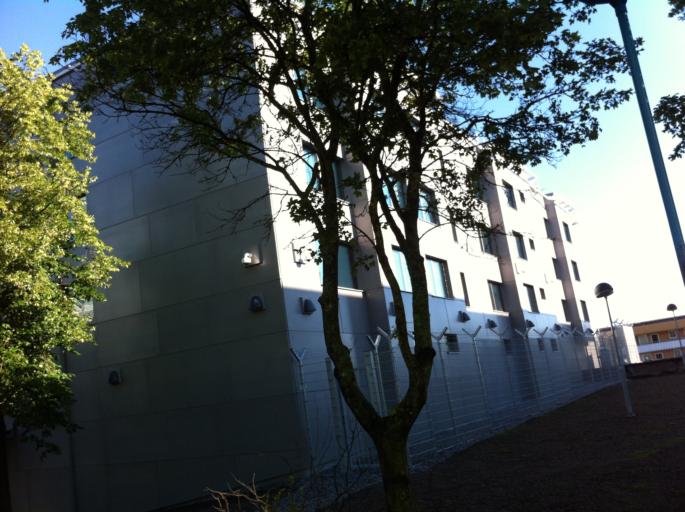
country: SE
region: Stockholm
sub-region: Stockholms Kommun
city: Kista
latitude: 59.3904
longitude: 17.9281
